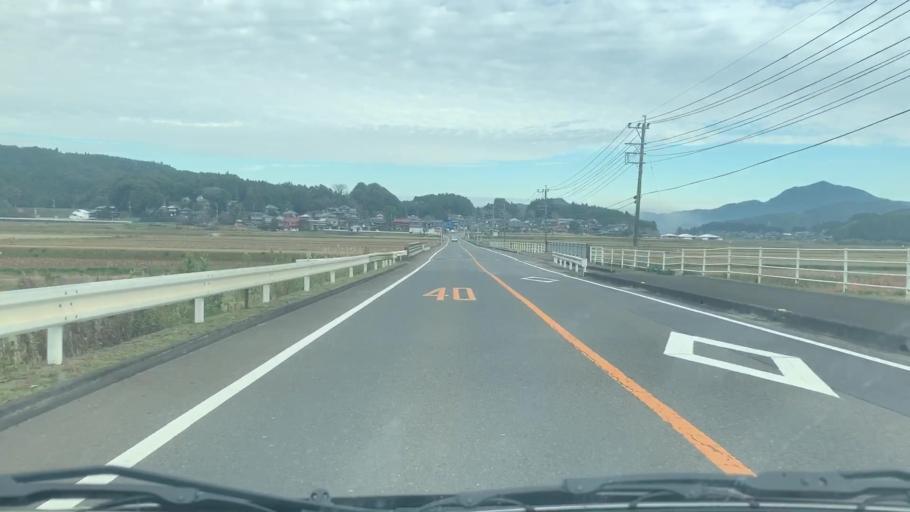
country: JP
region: Saga Prefecture
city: Takeocho-takeo
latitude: 33.2129
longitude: 129.9632
